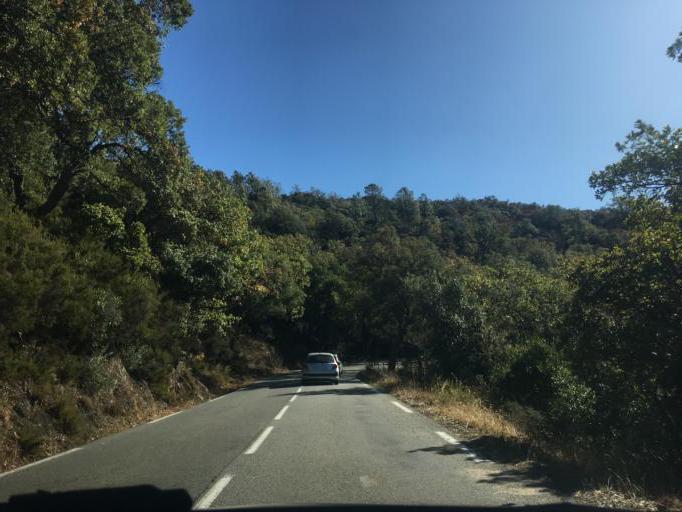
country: FR
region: Provence-Alpes-Cote d'Azur
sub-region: Departement du Var
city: La Garde-Freinet
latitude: 43.3293
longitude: 6.4614
